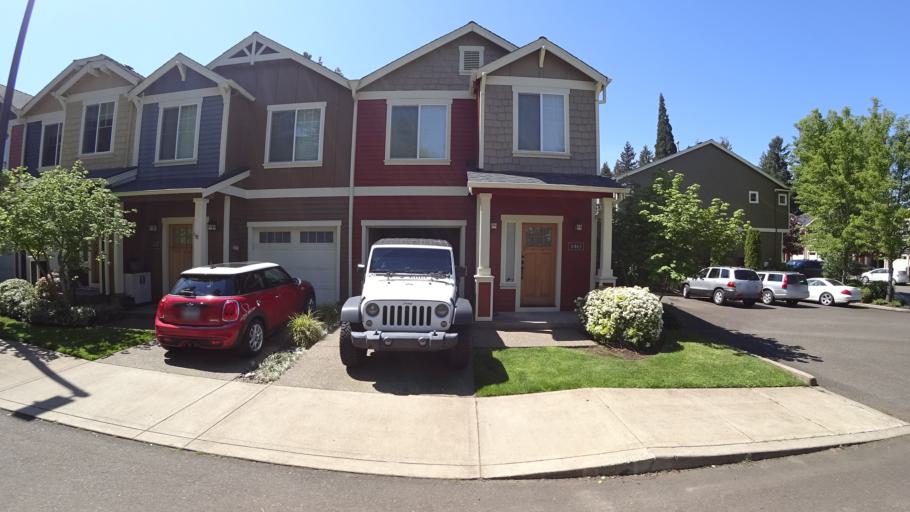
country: US
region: Oregon
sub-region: Washington County
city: King City
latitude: 45.4371
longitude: -122.8184
